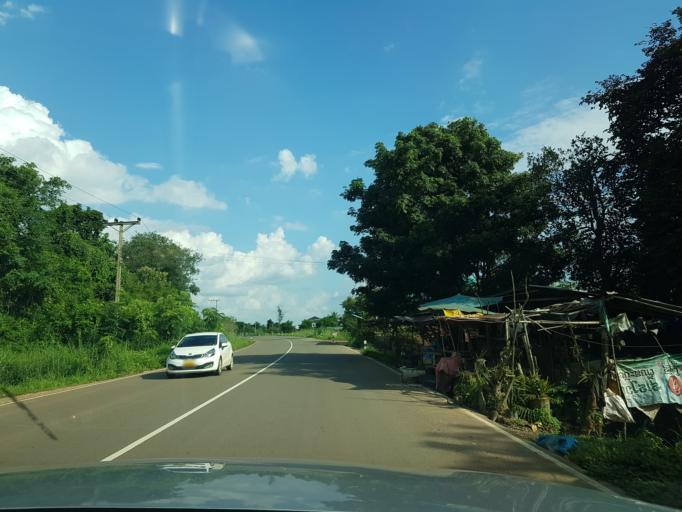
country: TH
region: Nong Khai
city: Pho Tak
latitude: 17.9842
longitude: 102.4422
